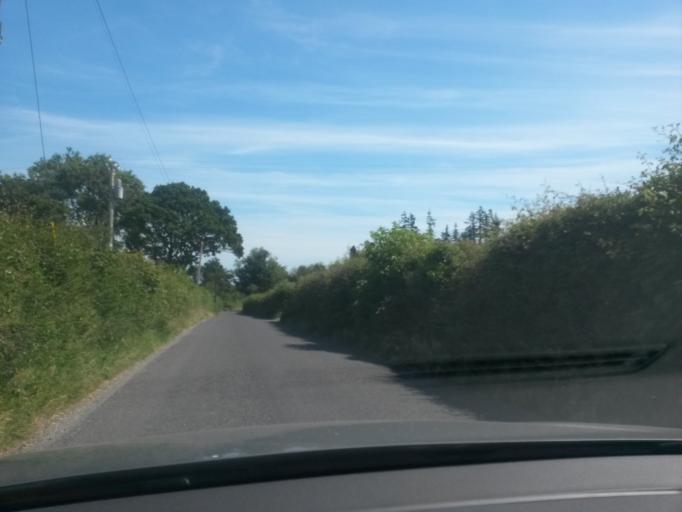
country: IE
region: Leinster
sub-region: Wicklow
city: Enniskerry
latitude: 53.1649
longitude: -6.1911
